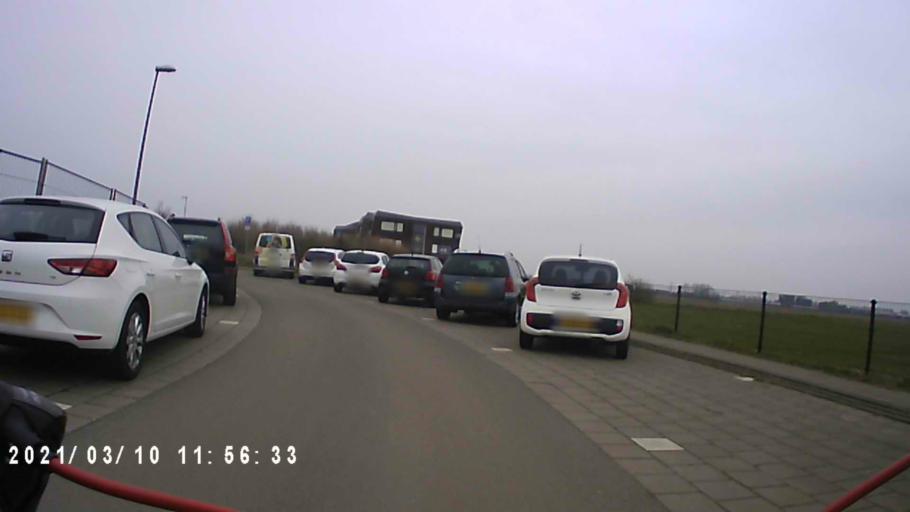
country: NL
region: Groningen
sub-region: Gemeente Zuidhorn
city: Aduard
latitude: 53.2294
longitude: 6.5058
